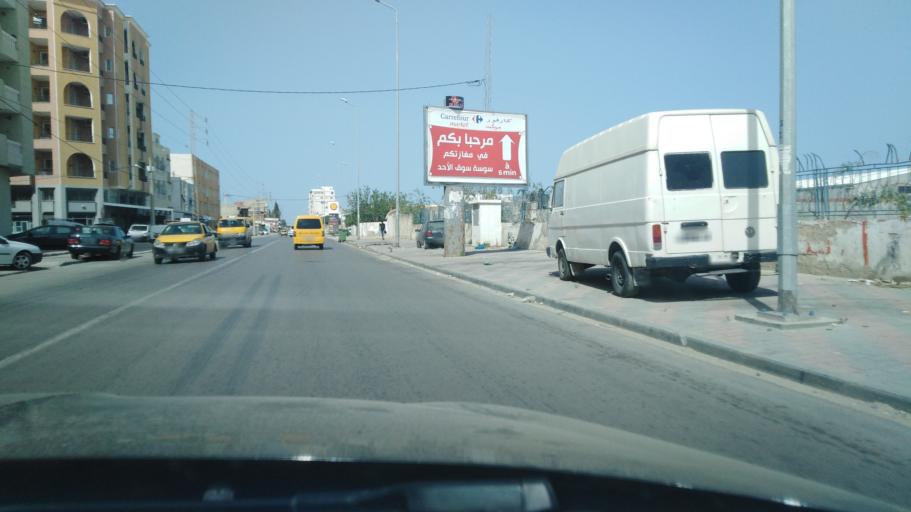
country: TN
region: Susah
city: Sousse
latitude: 35.8051
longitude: 10.6171
